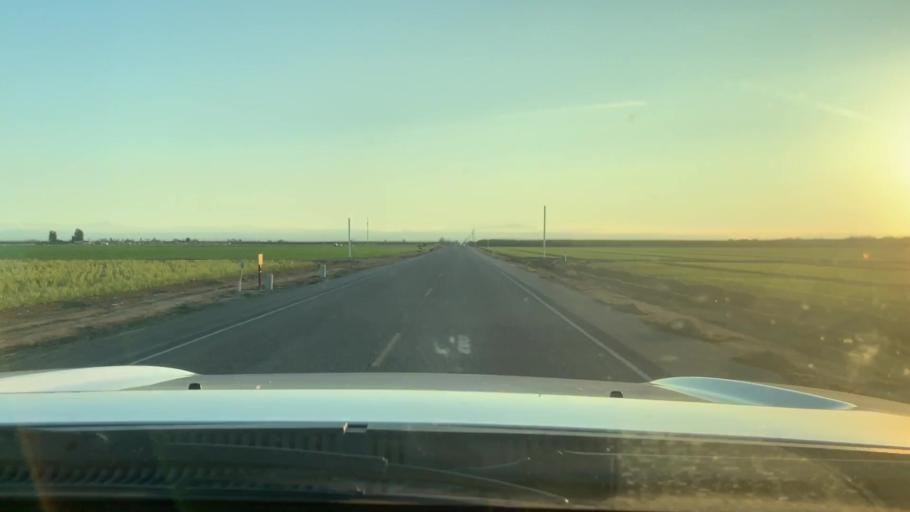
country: US
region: California
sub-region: Kern County
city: Wasco
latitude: 35.5001
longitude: -119.3821
